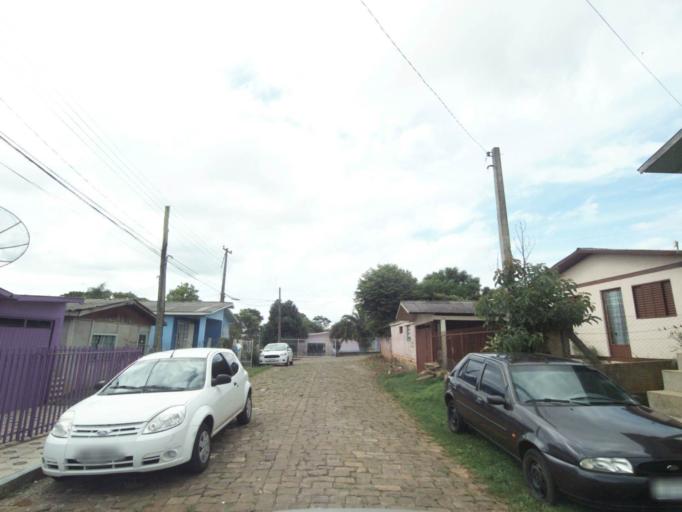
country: BR
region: Rio Grande do Sul
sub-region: Lagoa Vermelha
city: Lagoa Vermelha
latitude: -28.2093
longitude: -51.5388
